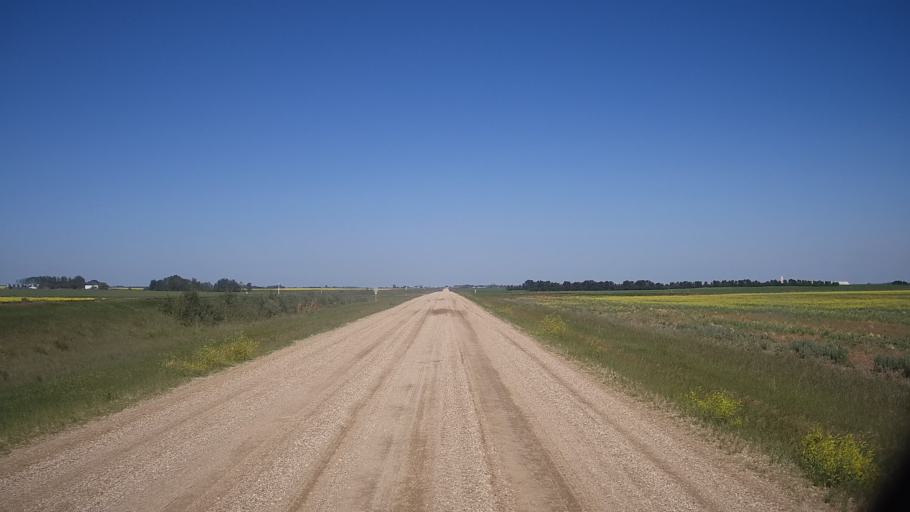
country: CA
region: Saskatchewan
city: Watrous
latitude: 51.8736
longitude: -106.0011
